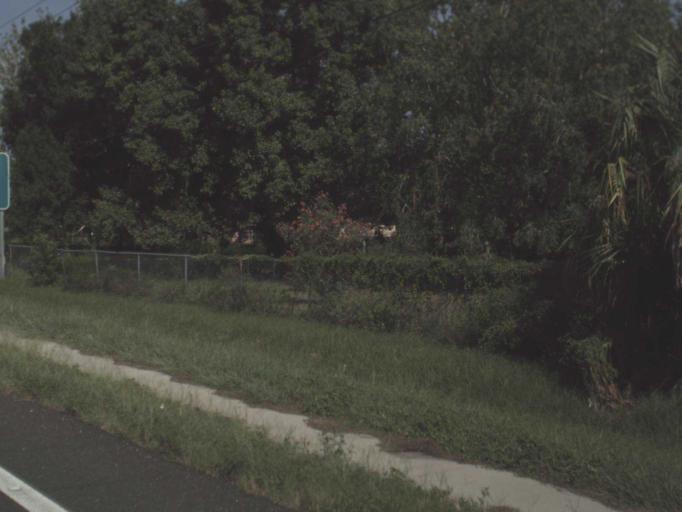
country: US
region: Florida
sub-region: Hillsborough County
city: Plant City
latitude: 27.9378
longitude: -82.1088
